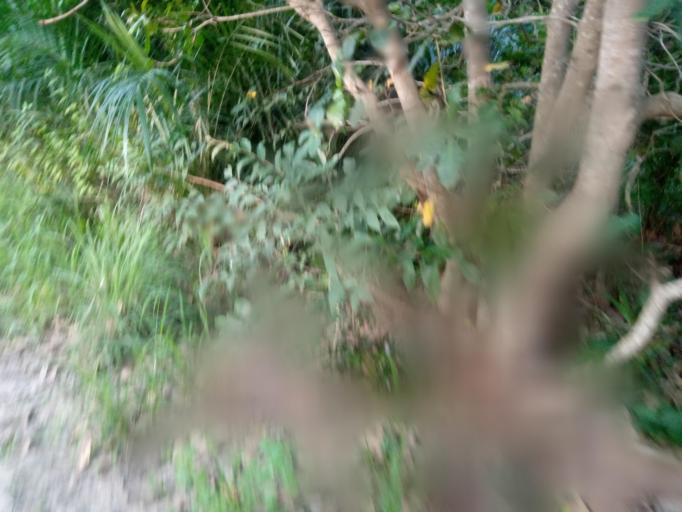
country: GM
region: Western
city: Gunjur
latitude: 13.0397
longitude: -16.7245
